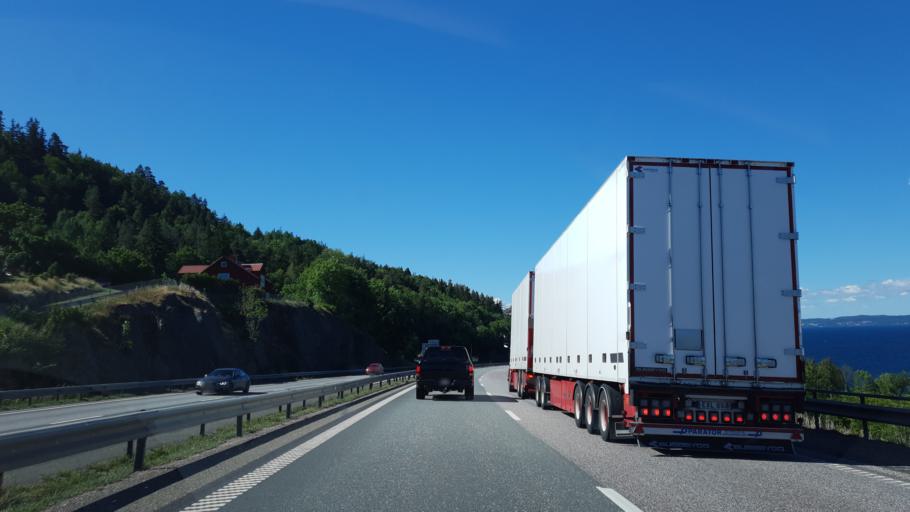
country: SE
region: Joenkoeping
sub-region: Jonkopings Kommun
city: Kaxholmen
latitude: 57.9159
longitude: 14.3102
